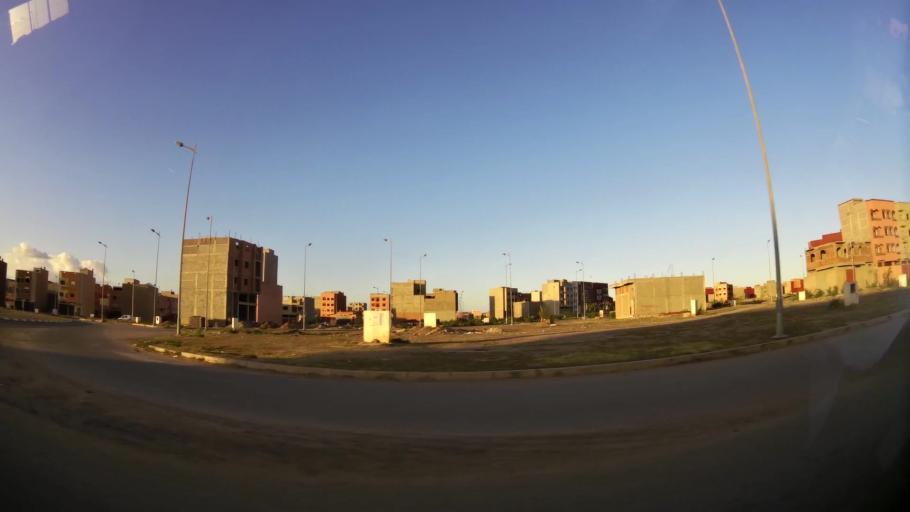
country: MA
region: Marrakech-Tensift-Al Haouz
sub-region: Kelaa-Des-Sraghna
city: Sidi Abdallah
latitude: 32.2389
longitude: -7.9455
